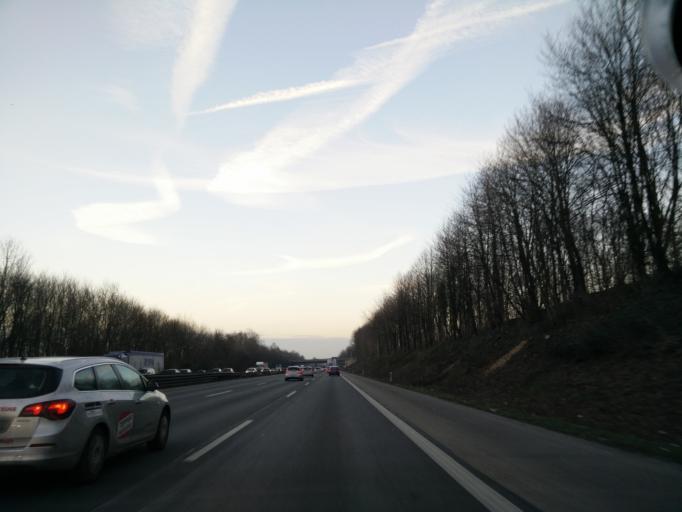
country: DE
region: North Rhine-Westphalia
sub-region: Regierungsbezirk Dusseldorf
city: Erkrath
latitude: 51.2711
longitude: 6.9114
